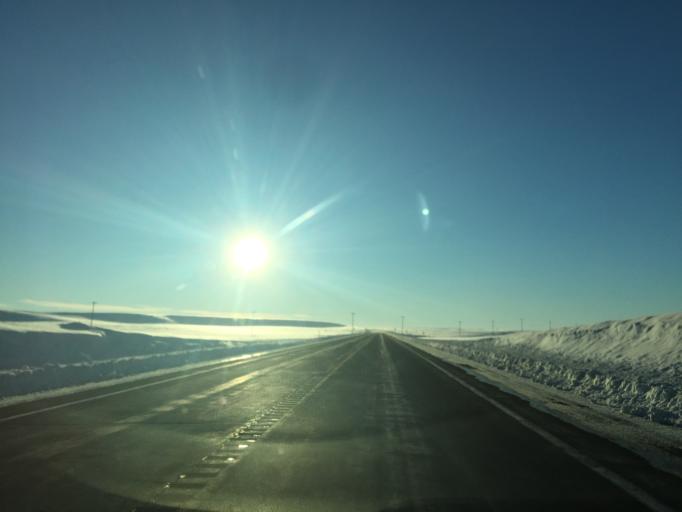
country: US
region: Washington
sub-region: Grant County
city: Soap Lake
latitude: 47.6143
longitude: -119.4763
